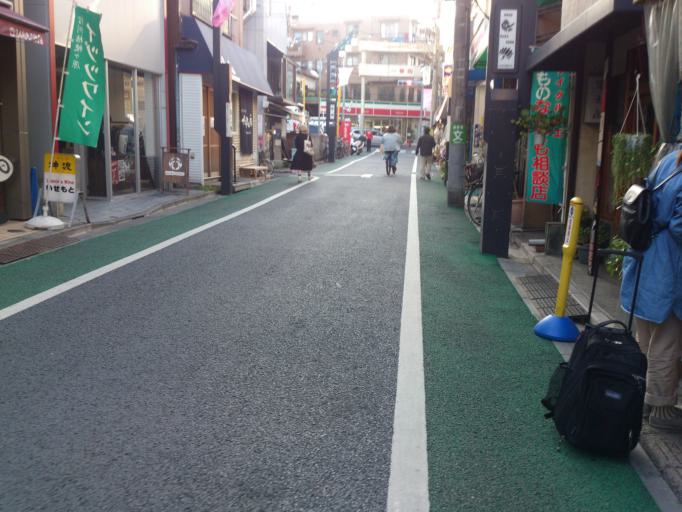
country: JP
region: Tokyo
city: Tokyo
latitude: 35.6648
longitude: 139.6660
